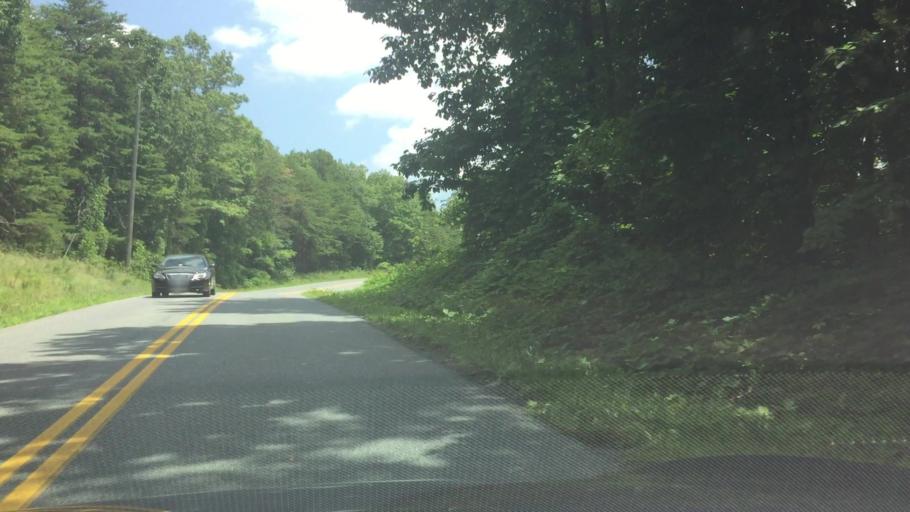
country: US
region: Virginia
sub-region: Appomattox County
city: Appomattox
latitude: 37.3199
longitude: -78.8493
